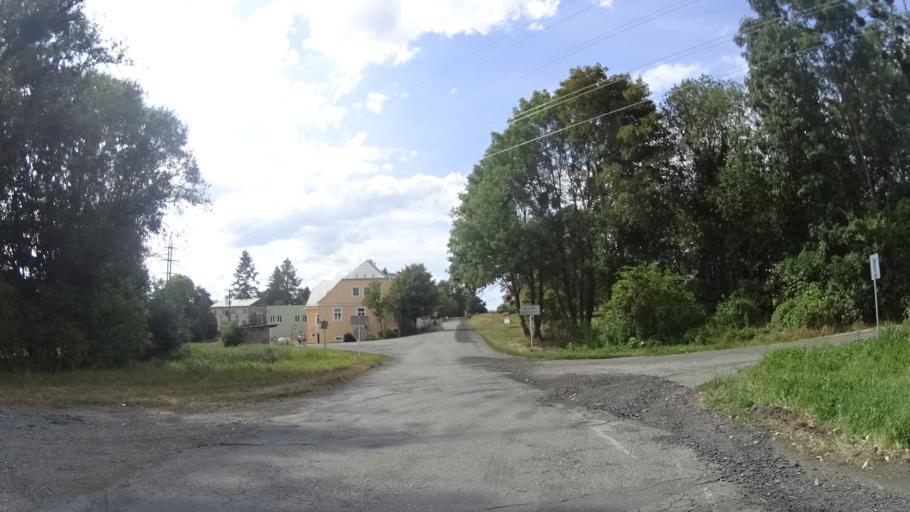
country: CZ
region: Olomoucky
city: Cervenka
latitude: 49.7205
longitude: 17.0329
